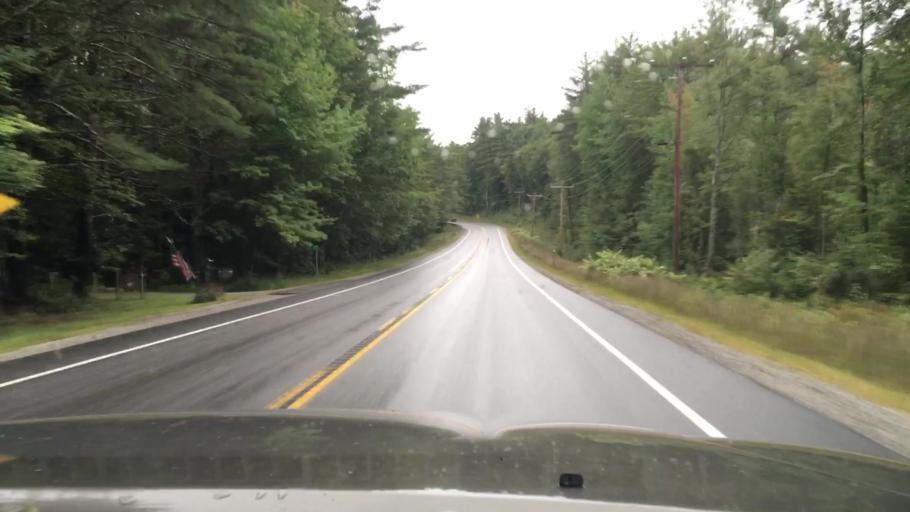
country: US
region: New Hampshire
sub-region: Hillsborough County
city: Antrim
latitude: 43.0931
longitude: -71.9660
